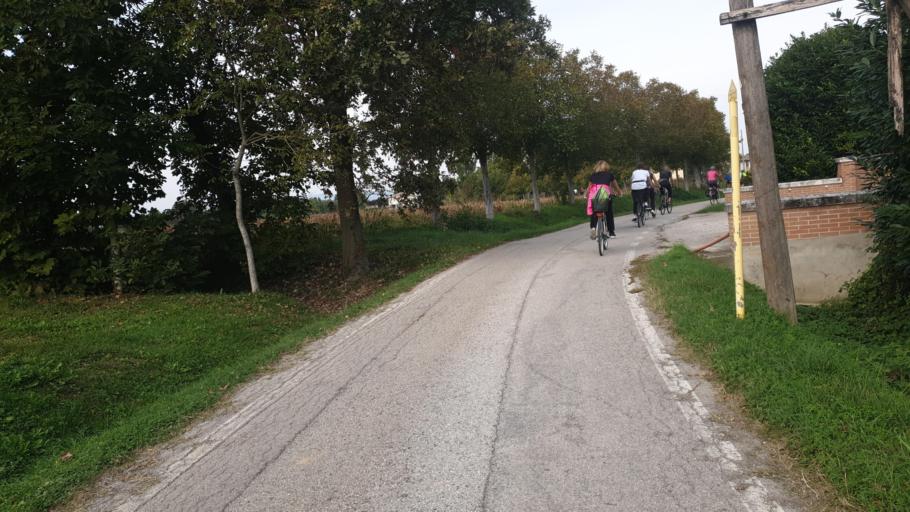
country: IT
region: Veneto
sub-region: Provincia di Padova
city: Cervarese Santa Croce
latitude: 45.4148
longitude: 11.7014
